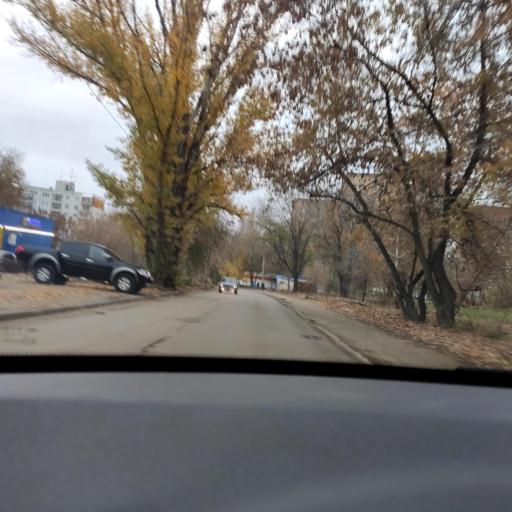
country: RU
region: Samara
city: Samara
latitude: 53.2444
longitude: 50.2180
